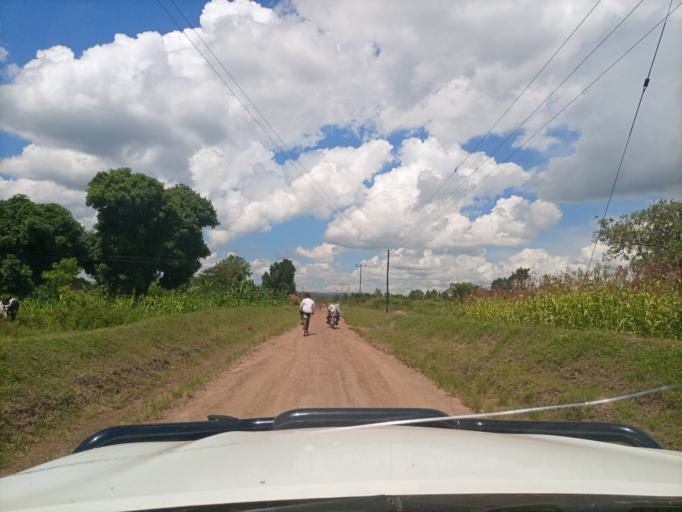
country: UG
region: Eastern Region
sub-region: Tororo District
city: Tororo
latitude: 0.6468
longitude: 33.9960
